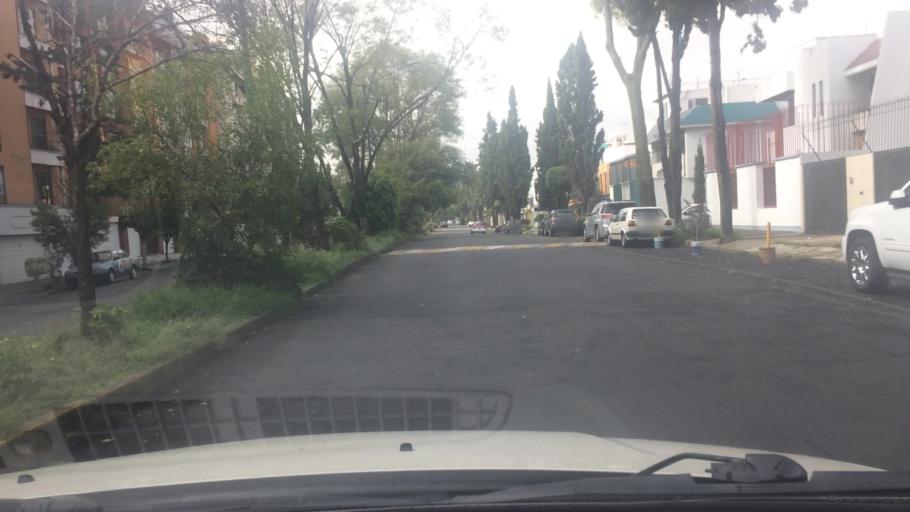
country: MX
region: Mexico City
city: Colonia Nativitas
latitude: 19.3485
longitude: -99.1264
